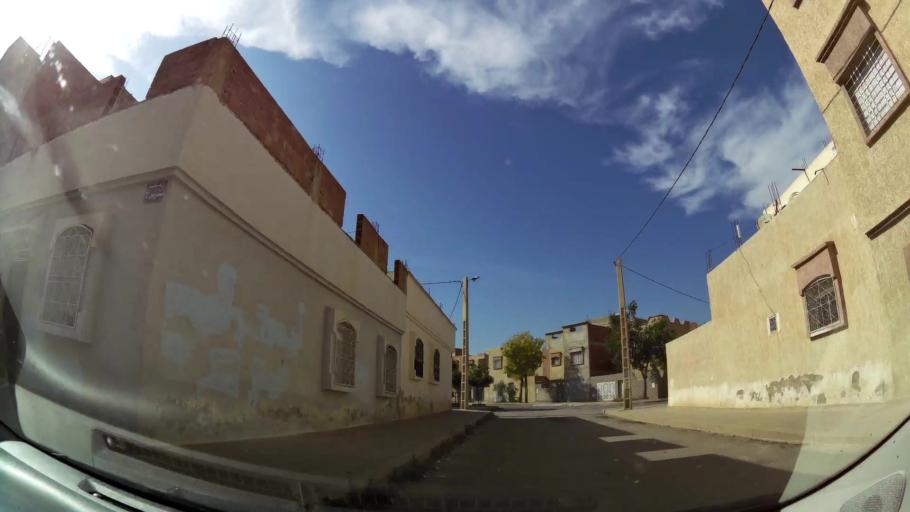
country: MA
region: Oriental
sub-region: Oujda-Angad
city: Oujda
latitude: 34.7116
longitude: -1.8821
